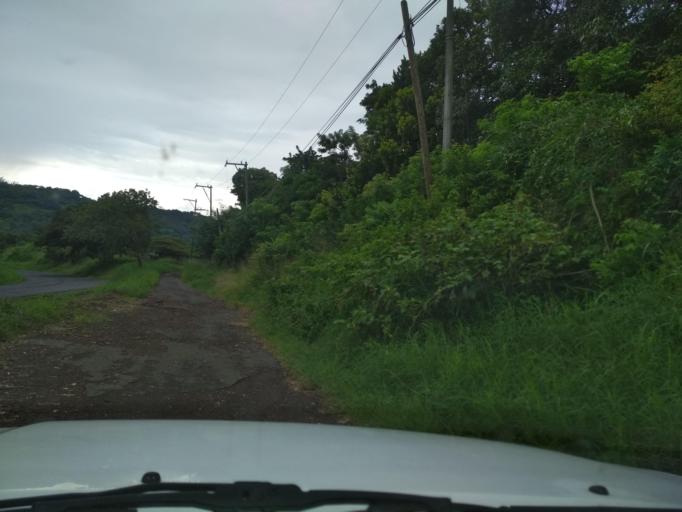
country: MX
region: Veracruz
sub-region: San Andres Tuxtla
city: Los Pinos
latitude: 18.4466
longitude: -95.2325
